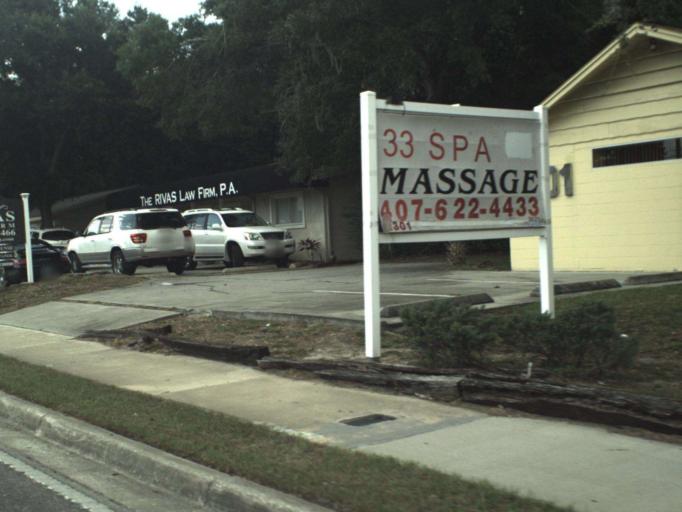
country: US
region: Florida
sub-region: Orange County
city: Eatonville
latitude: 28.6059
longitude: -81.3803
